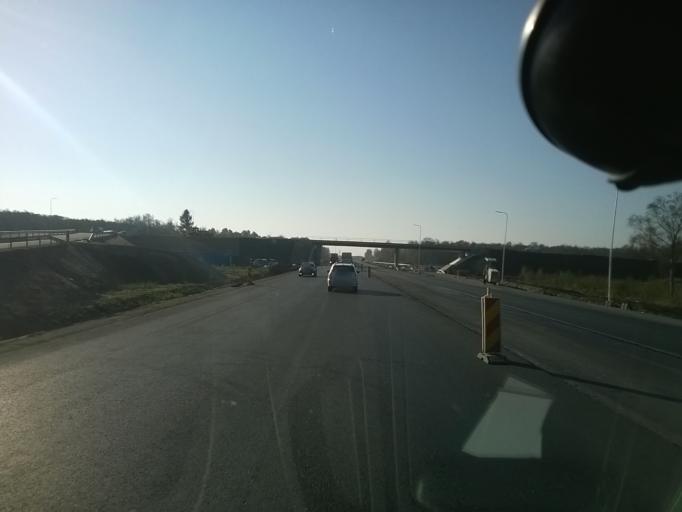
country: EE
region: Harju
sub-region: Rae vald
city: Jueri
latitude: 59.3736
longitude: 24.9110
